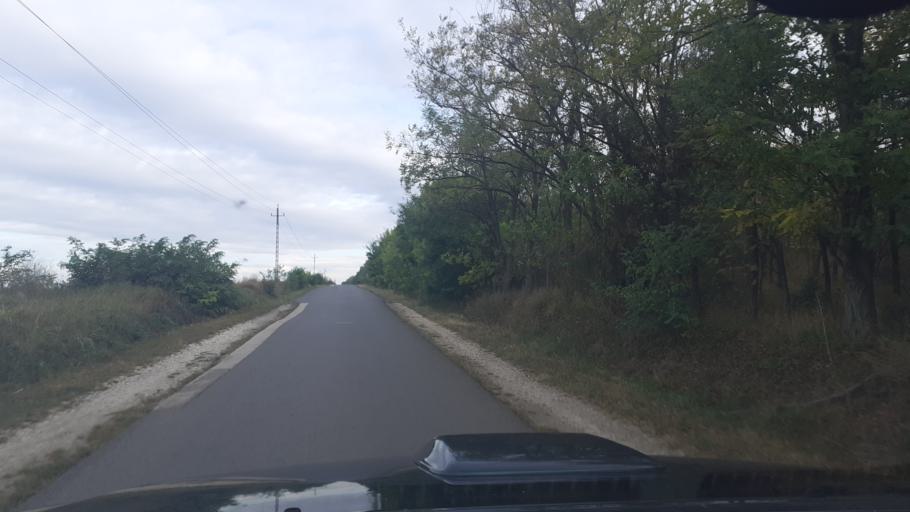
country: HU
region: Fejer
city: Baracs
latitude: 46.9290
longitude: 18.8739
